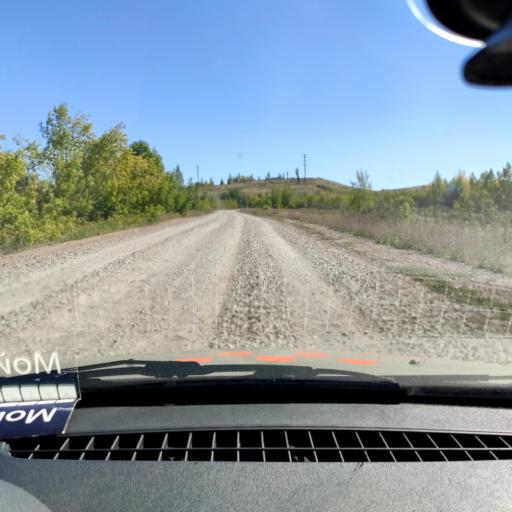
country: RU
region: Bashkortostan
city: Yermolayevo
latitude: 52.7492
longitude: 55.8303
